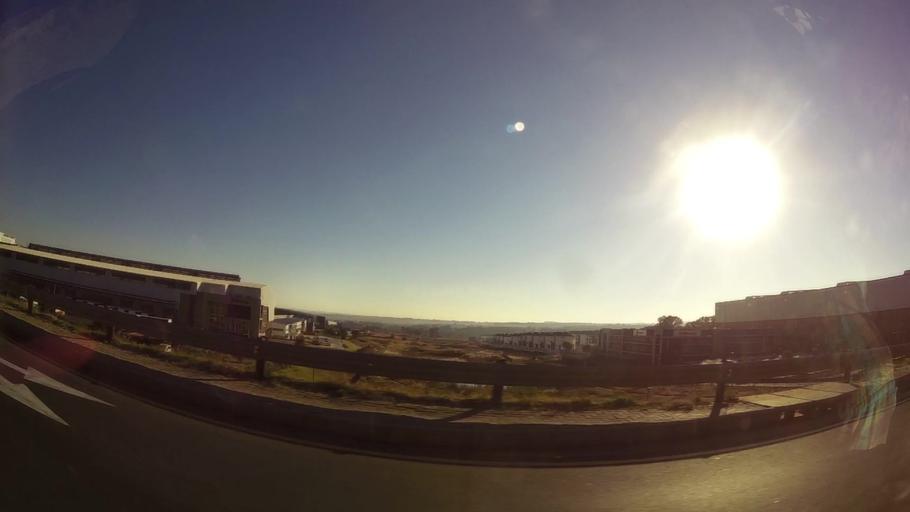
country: ZA
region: Gauteng
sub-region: City of Johannesburg Metropolitan Municipality
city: Modderfontein
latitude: -26.1052
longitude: 28.1415
